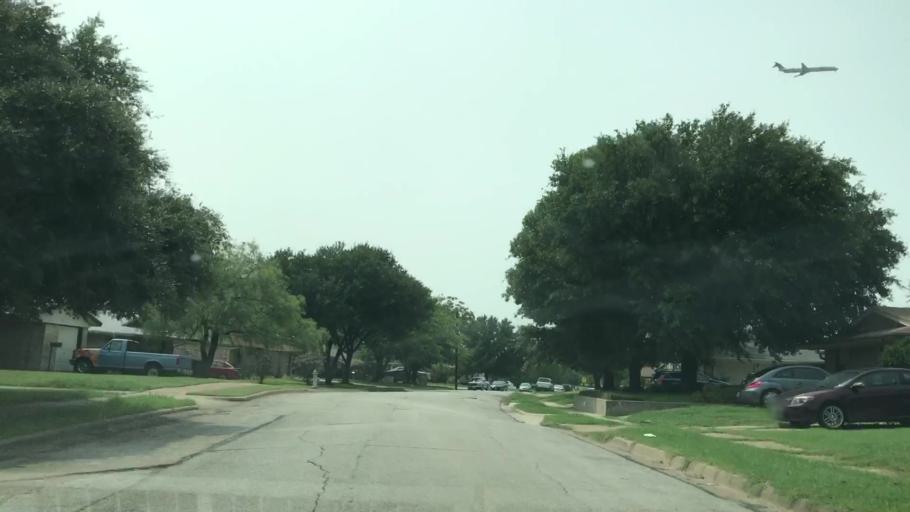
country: US
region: Texas
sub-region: Dallas County
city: Irving
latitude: 32.8395
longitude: -97.0032
